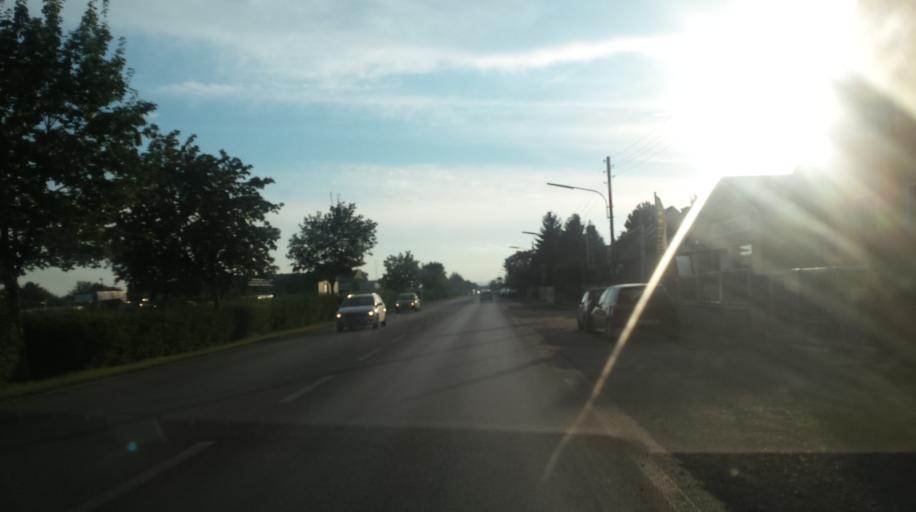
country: AT
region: Lower Austria
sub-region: Politischer Bezirk Ganserndorf
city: Parbasdorf
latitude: 48.3130
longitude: 16.6163
